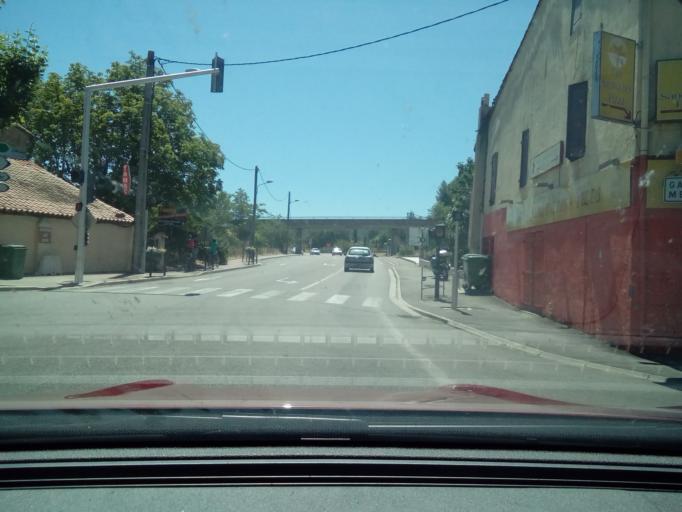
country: FR
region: Provence-Alpes-Cote d'Azur
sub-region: Departement des Bouches-du-Rhone
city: Fuveau
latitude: 43.4783
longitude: 5.5380
